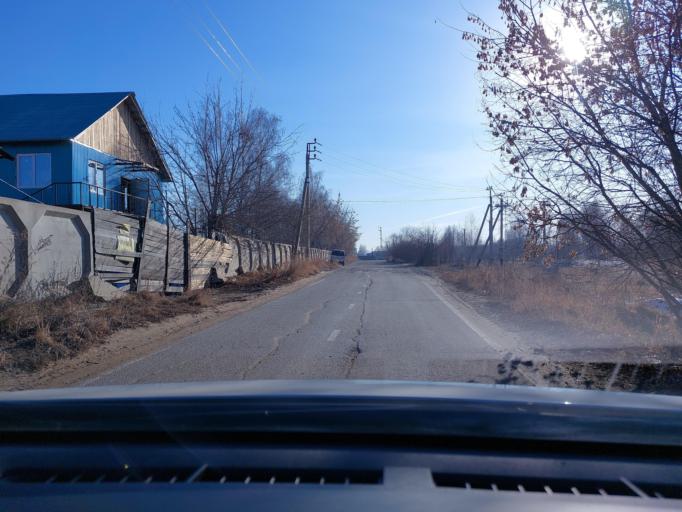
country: RU
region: Irkutsk
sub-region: Irkutskiy Rayon
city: Irkutsk
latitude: 52.3099
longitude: 104.2715
